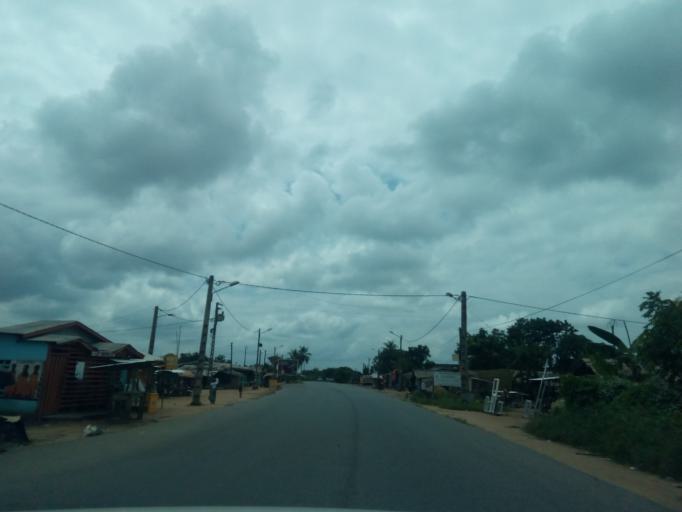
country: CI
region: Sud-Comoe
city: Aboisso
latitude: 5.4577
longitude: -3.2557
